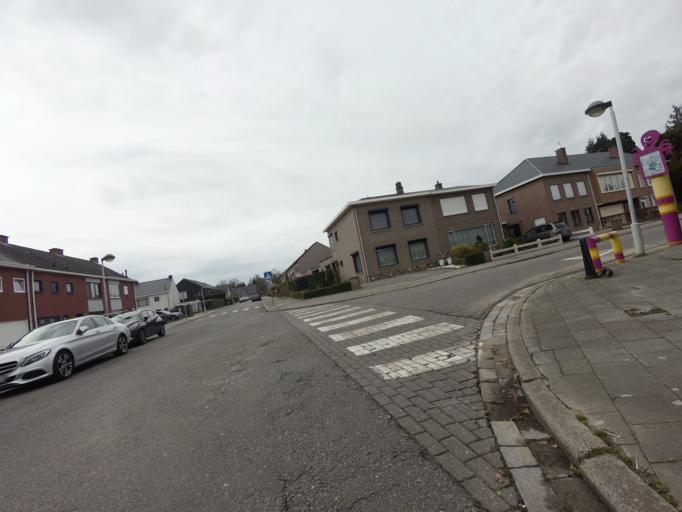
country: BE
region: Flanders
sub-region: Provincie Antwerpen
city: Lier
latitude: 51.1231
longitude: 4.5506
